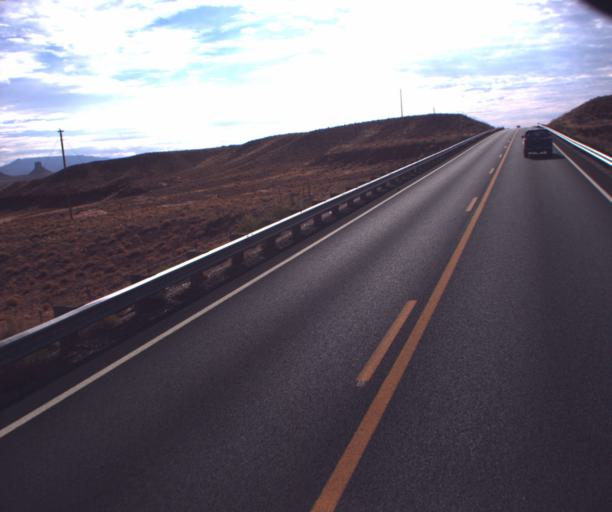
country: US
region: Arizona
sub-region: Apache County
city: Many Farms
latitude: 36.6022
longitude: -109.5706
